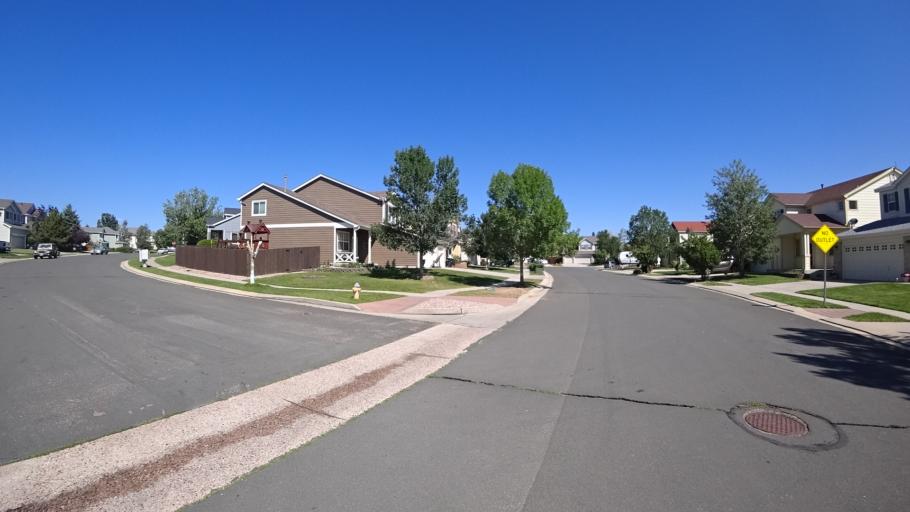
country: US
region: Colorado
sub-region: El Paso County
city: Black Forest
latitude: 38.9447
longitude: -104.7445
